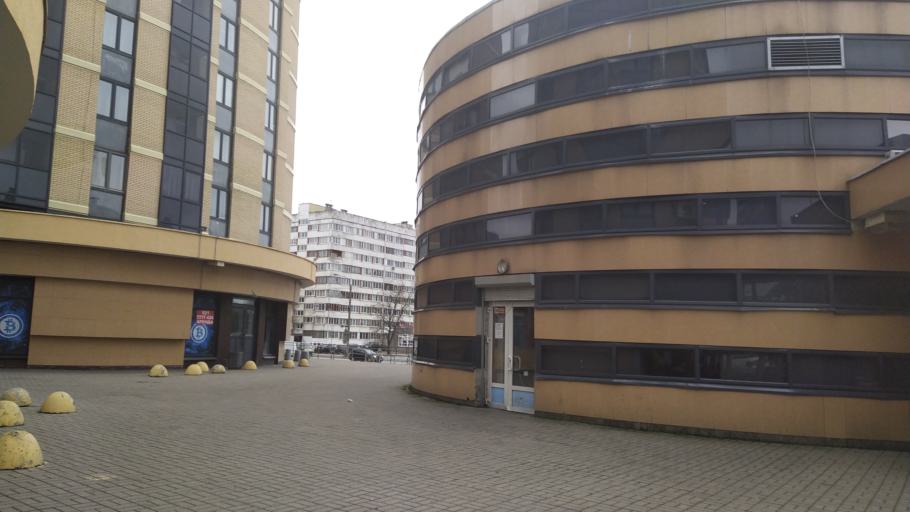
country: RU
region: St.-Petersburg
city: Komendantsky aerodrom
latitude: 60.0121
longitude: 30.2789
